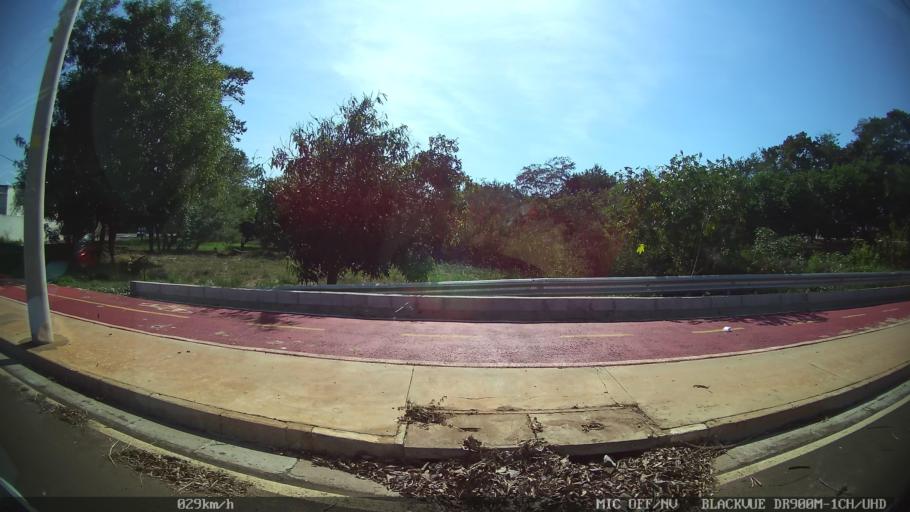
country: BR
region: Sao Paulo
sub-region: Sao Jose Do Rio Preto
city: Sao Jose do Rio Preto
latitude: -20.7885
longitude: -49.4136
